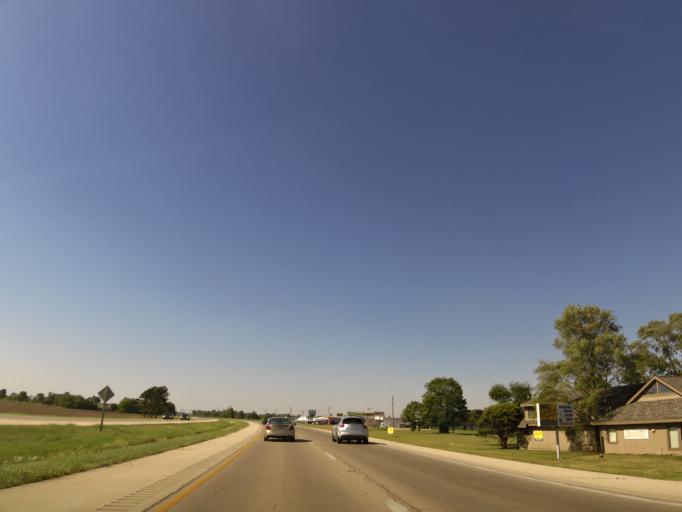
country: US
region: Illinois
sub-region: Winnebago County
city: Roscoe
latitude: 42.4311
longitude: -89.0162
